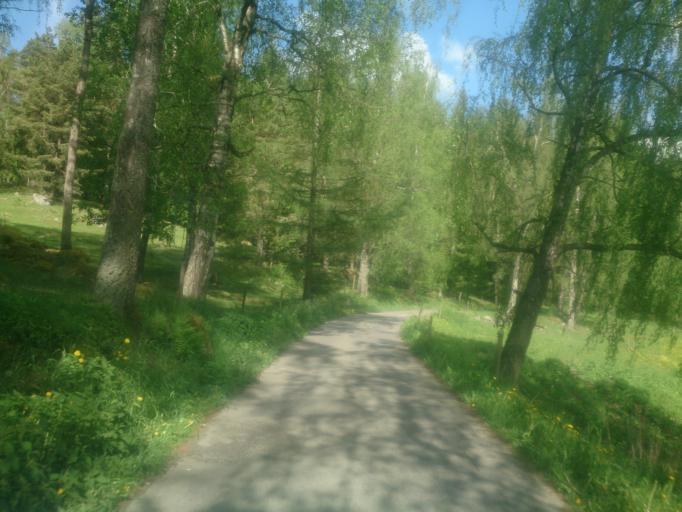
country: SE
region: OEstergoetland
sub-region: Atvidabergs Kommun
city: Atvidaberg
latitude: 58.2992
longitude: 16.0787
